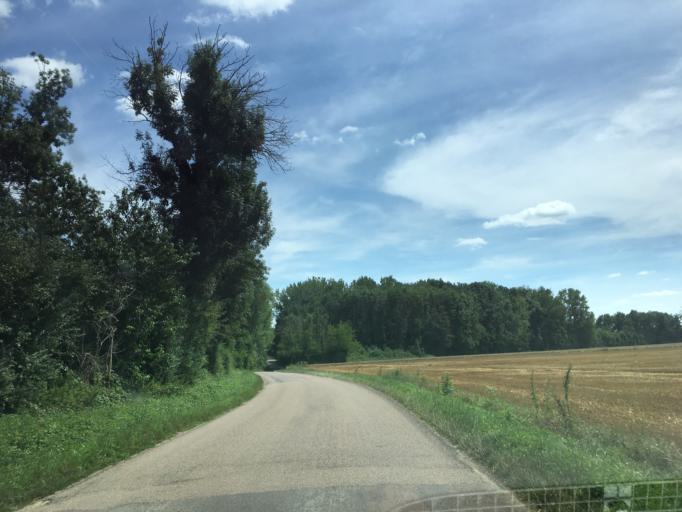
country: FR
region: Bourgogne
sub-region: Departement de l'Yonne
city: Fleury-la-Vallee
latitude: 47.8649
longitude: 3.4393
